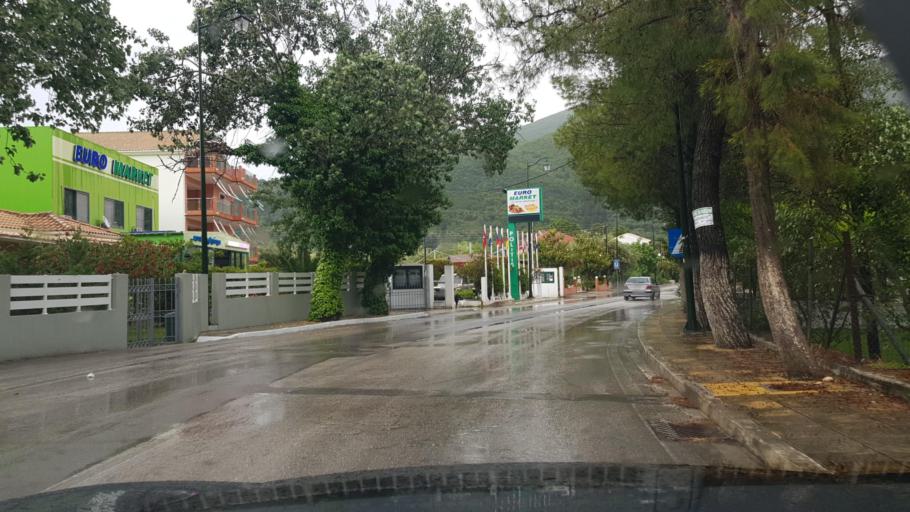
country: GR
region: Ionian Islands
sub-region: Lefkada
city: Nidri
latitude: 38.6316
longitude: 20.6062
